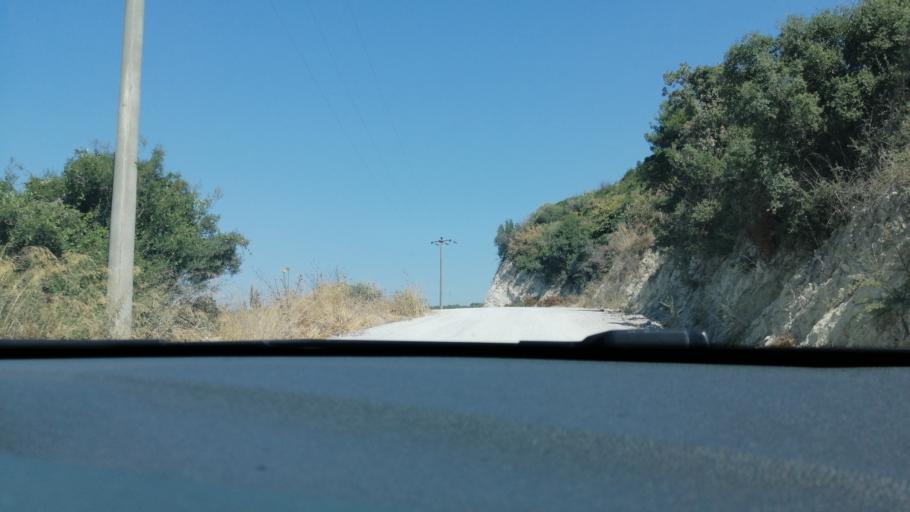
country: TR
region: Aydin
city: Davutlar
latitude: 37.7822
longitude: 27.3142
